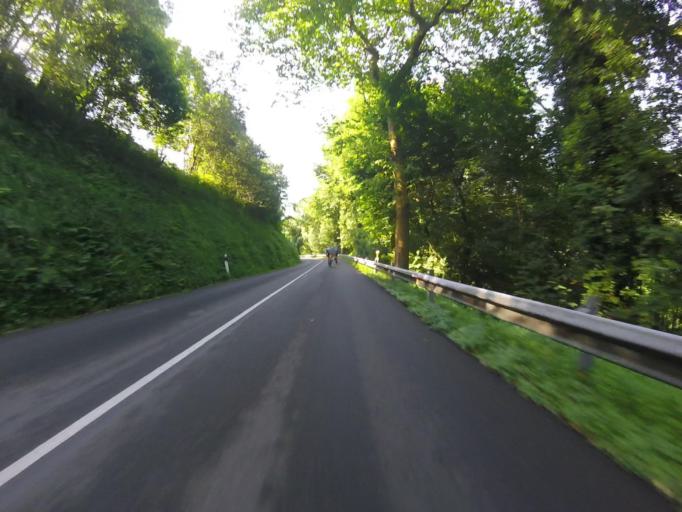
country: ES
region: Basque Country
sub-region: Provincia de Guipuzcoa
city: Asteasu
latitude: 43.2039
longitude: -2.1092
